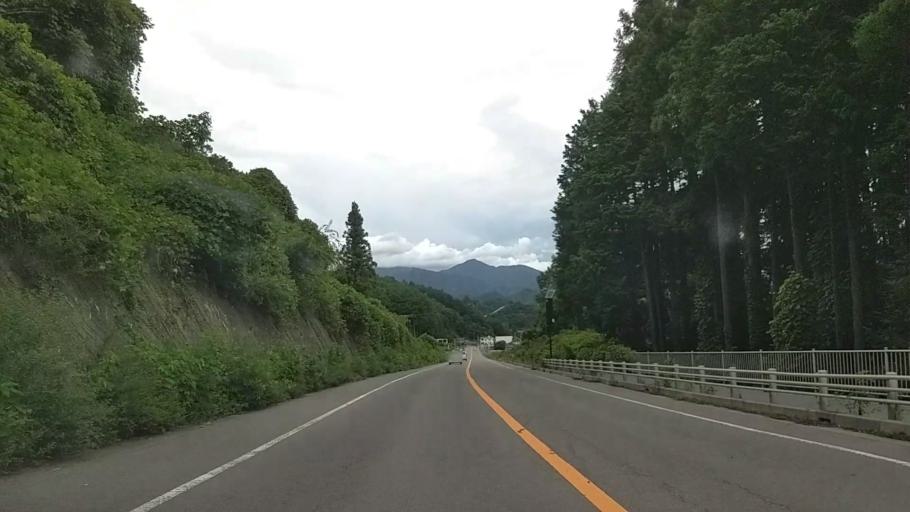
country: JP
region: Yamanashi
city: Otsuki
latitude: 35.5644
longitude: 138.9331
